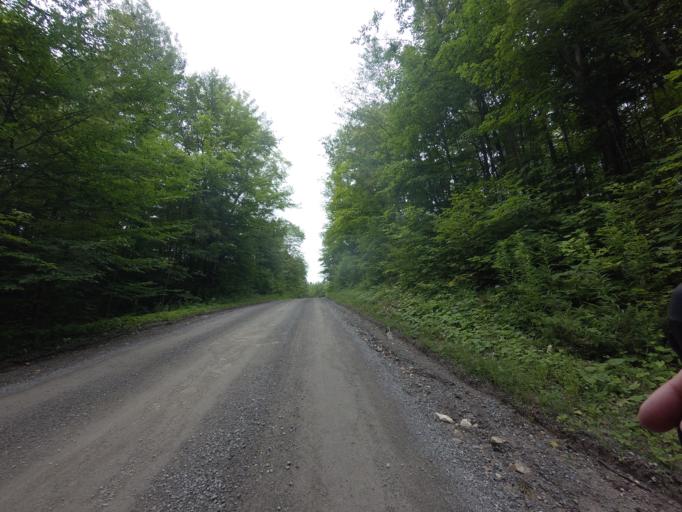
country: CA
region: Ontario
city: Kingston
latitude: 44.5711
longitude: -76.5475
